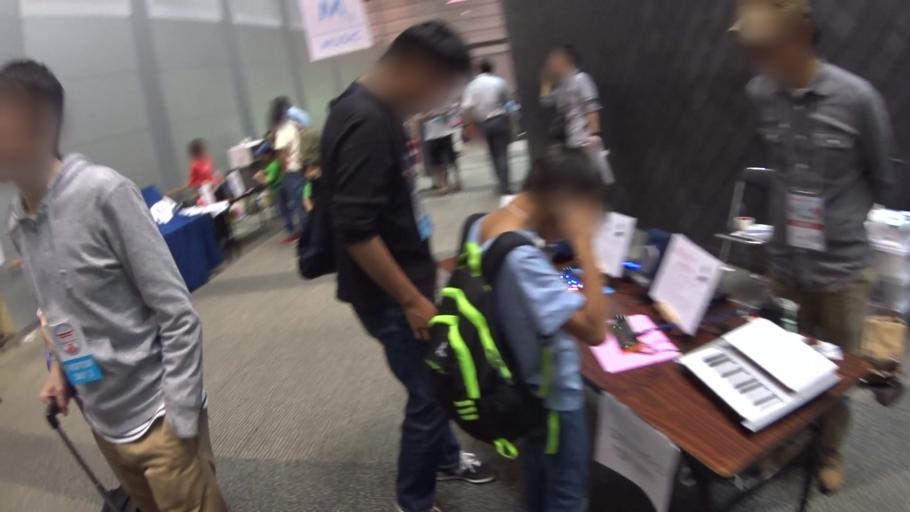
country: JP
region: Nara
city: Nara-shi
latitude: 34.7454
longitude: 135.7810
